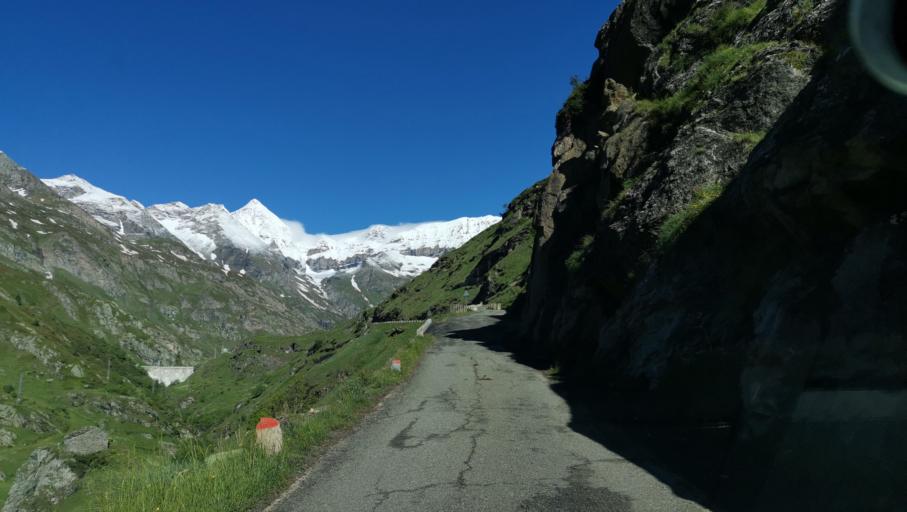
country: IT
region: Piedmont
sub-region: Provincia di Torino
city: Chianocco
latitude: 45.2073
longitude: 7.1532
